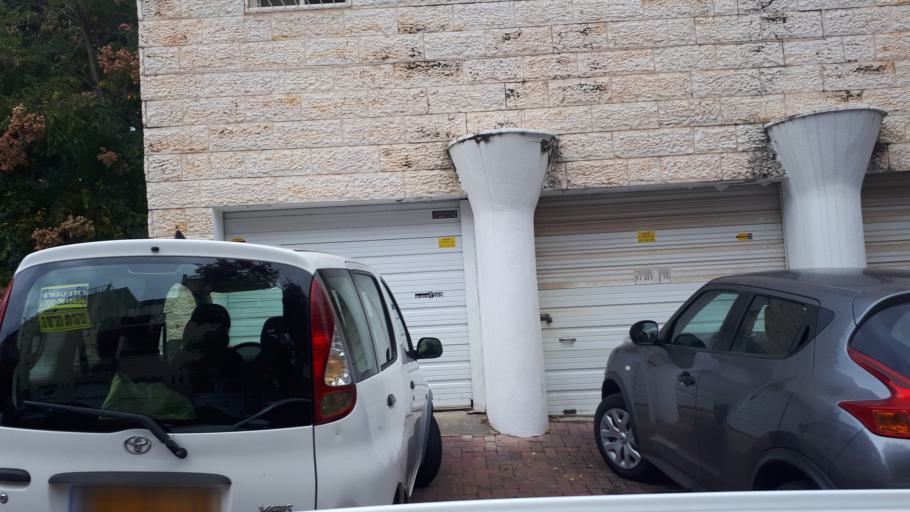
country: IL
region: Central District
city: Modiin
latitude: 31.9065
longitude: 35.0140
